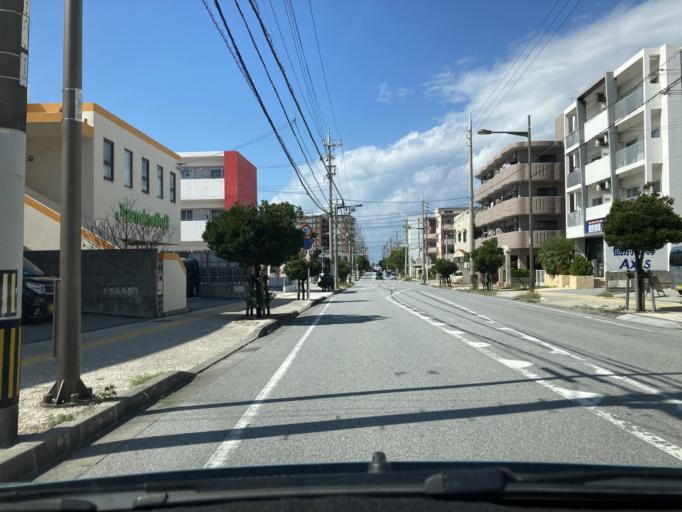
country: JP
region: Okinawa
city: Ginowan
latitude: 26.2731
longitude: 127.7333
